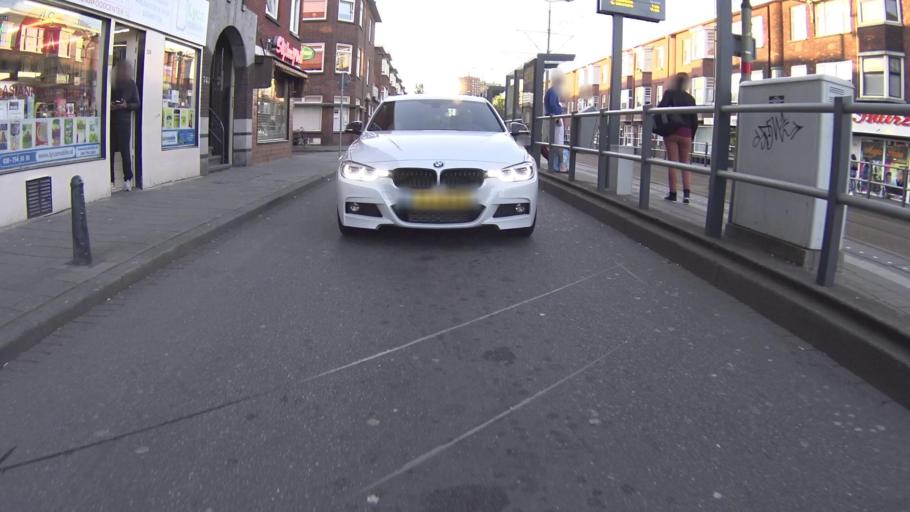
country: NL
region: South Holland
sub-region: Gemeente Rijswijk
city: Rijswijk
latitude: 52.0609
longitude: 4.3268
